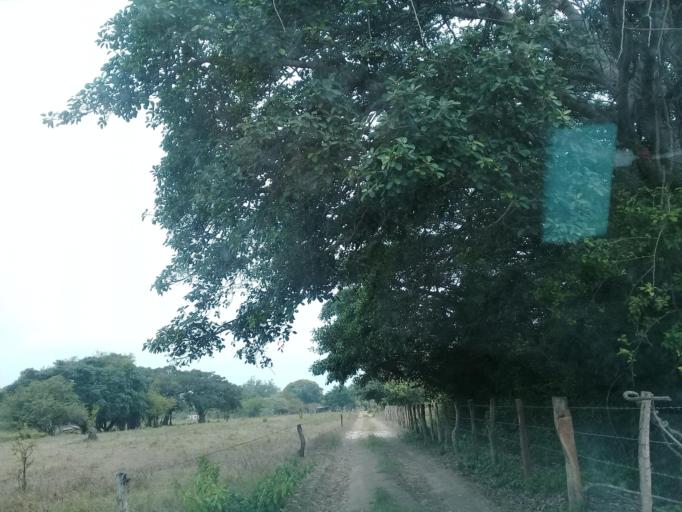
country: MX
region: Veracruz
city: El Tejar
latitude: 19.0433
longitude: -96.1907
